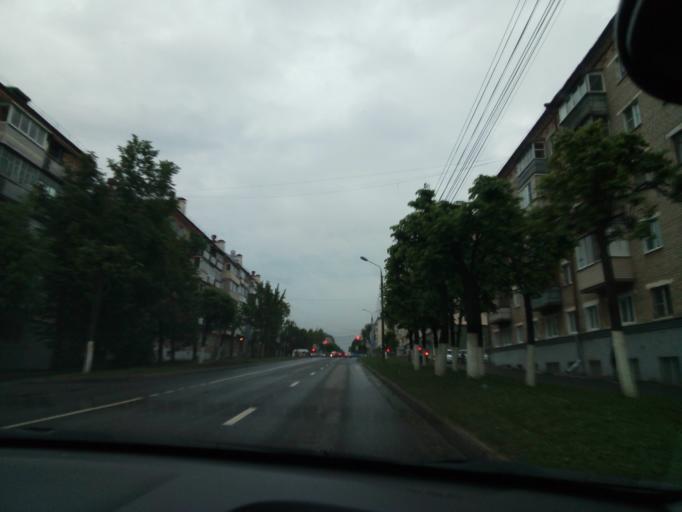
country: RU
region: Chuvashia
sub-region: Cheboksarskiy Rayon
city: Cheboksary
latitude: 56.1257
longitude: 47.2552
